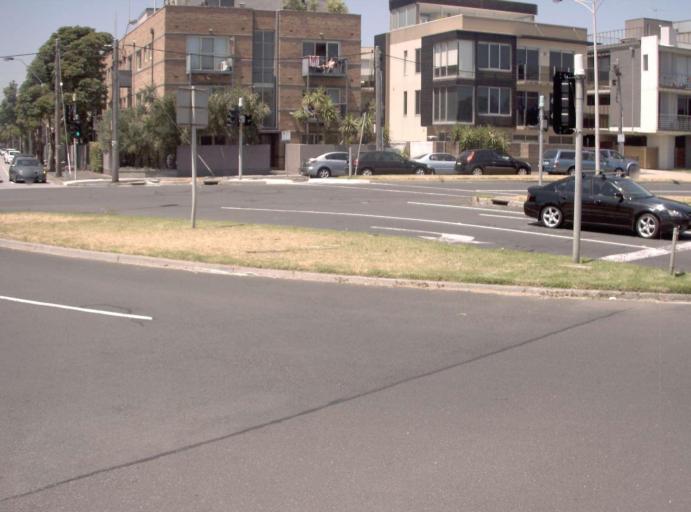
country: AU
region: Victoria
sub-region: Port Phillip
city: Elwood
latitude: -37.8817
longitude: 144.9780
